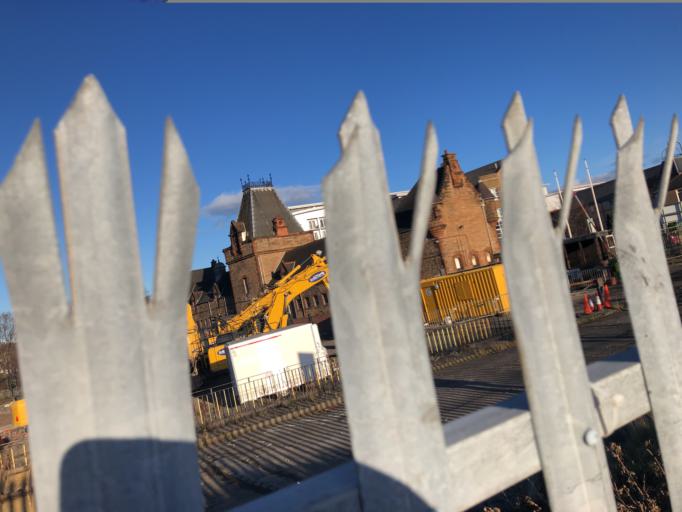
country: GB
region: Scotland
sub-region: Edinburgh
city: Edinburgh
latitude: 55.9665
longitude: -3.1896
